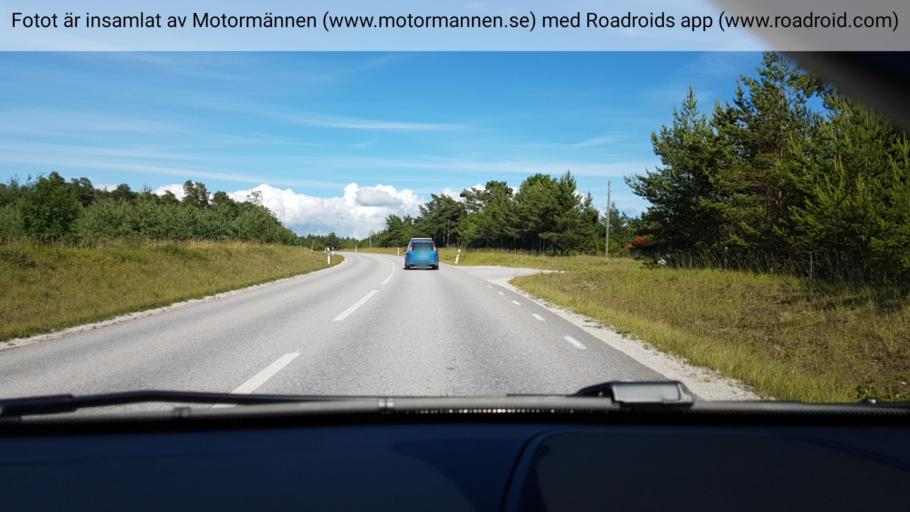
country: SE
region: Gotland
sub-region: Gotland
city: Slite
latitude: 57.7435
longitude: 18.6425
